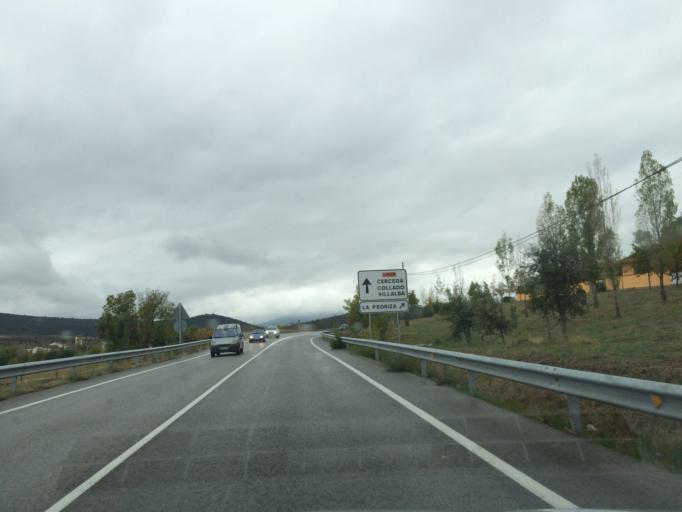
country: ES
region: Madrid
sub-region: Provincia de Madrid
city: Manzanares el Real
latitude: 40.7247
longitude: -3.8706
